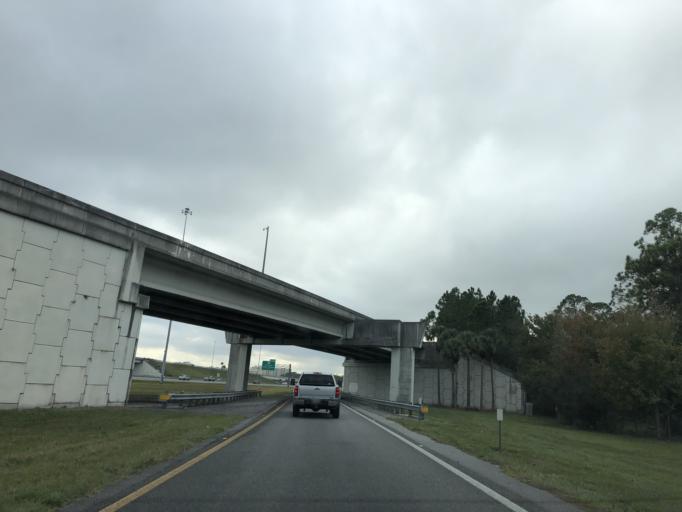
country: US
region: Florida
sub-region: Osceola County
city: Celebration
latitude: 28.3533
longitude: -81.5277
